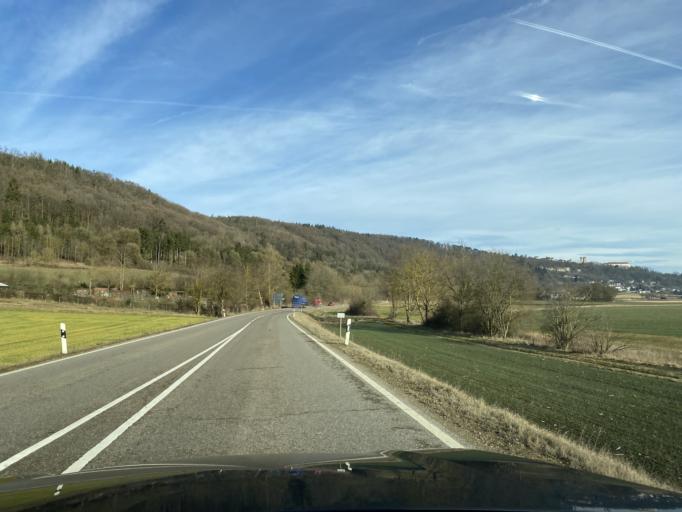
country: DE
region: Bavaria
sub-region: Upper Bavaria
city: Denkendorf
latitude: 49.0186
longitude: 11.4483
